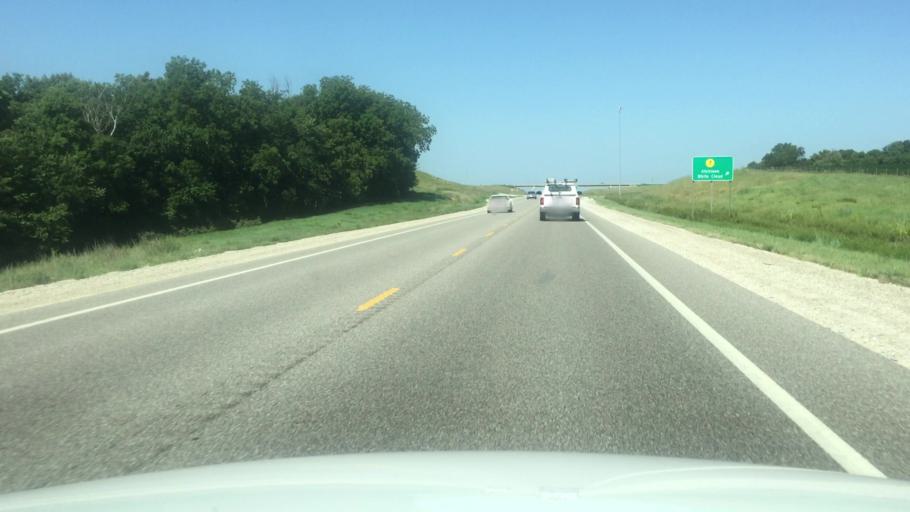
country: US
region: Kansas
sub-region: Doniphan County
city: Troy
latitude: 39.7979
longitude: -95.1351
